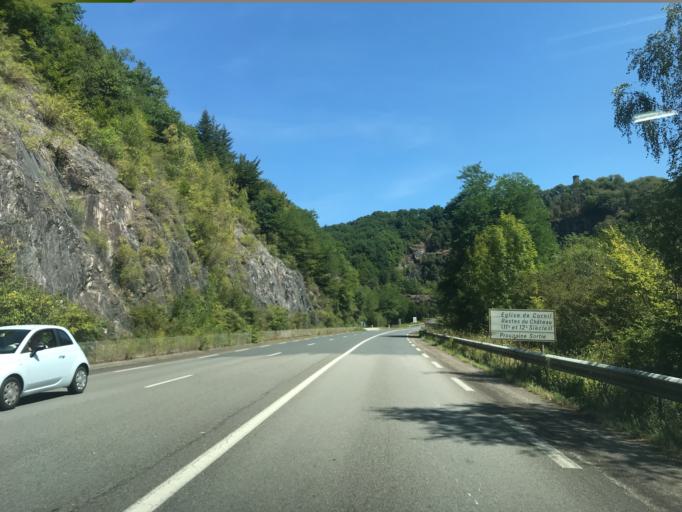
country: FR
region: Limousin
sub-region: Departement de la Correze
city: Cornil
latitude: 45.2111
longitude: 1.6844
